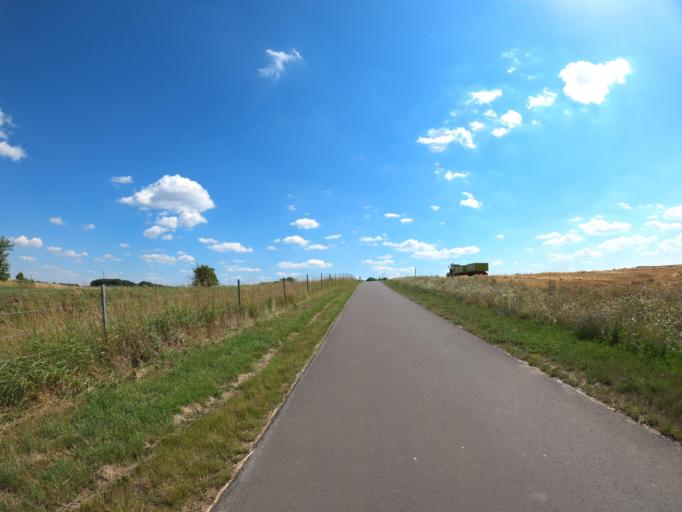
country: DE
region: Brandenburg
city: Mescherin
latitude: 53.2790
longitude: 14.4202
